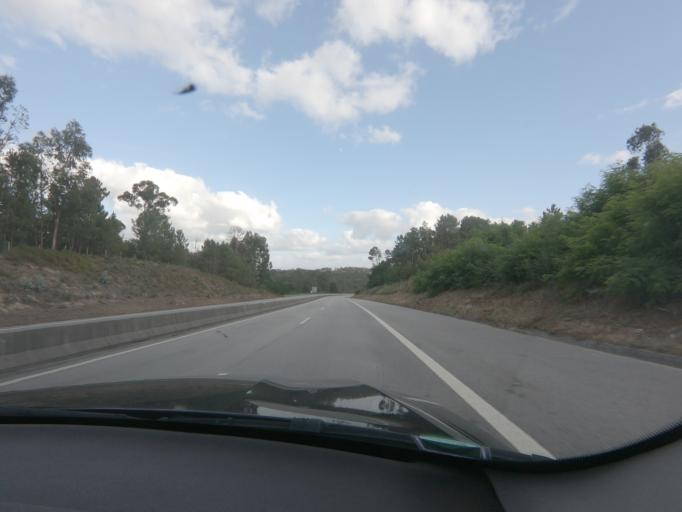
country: PT
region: Viseu
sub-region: Viseu
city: Abraveses
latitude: 40.6602
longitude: -7.9697
